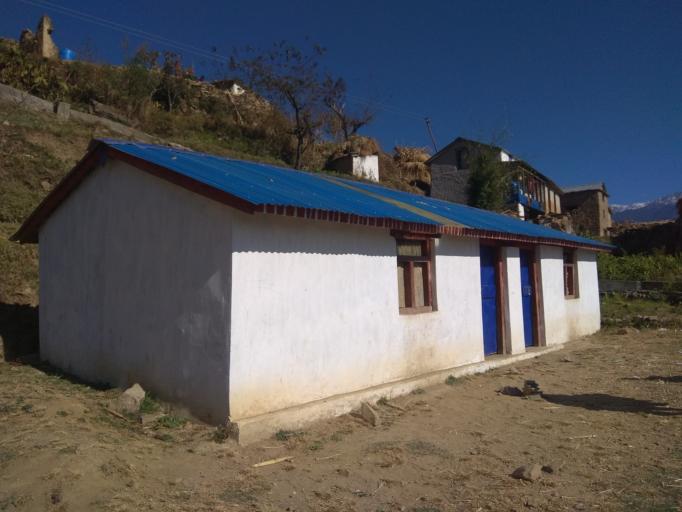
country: NP
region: Far Western
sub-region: Seti Zone
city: Achham
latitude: 29.2561
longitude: 81.6352
